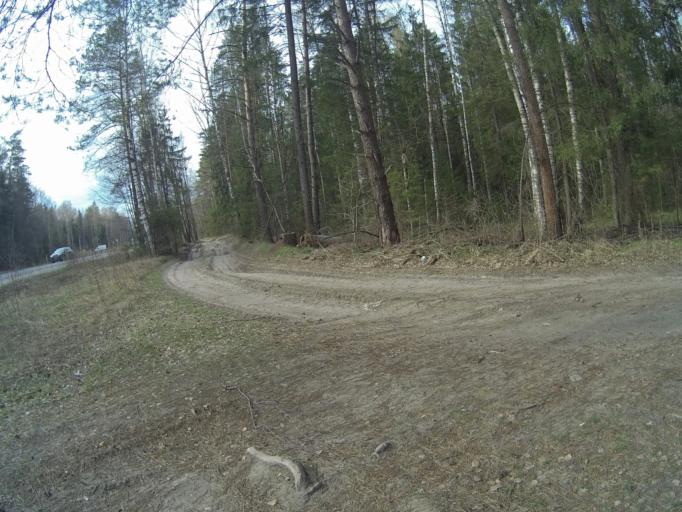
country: RU
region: Vladimir
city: Kommunar
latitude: 56.0178
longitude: 40.5836
